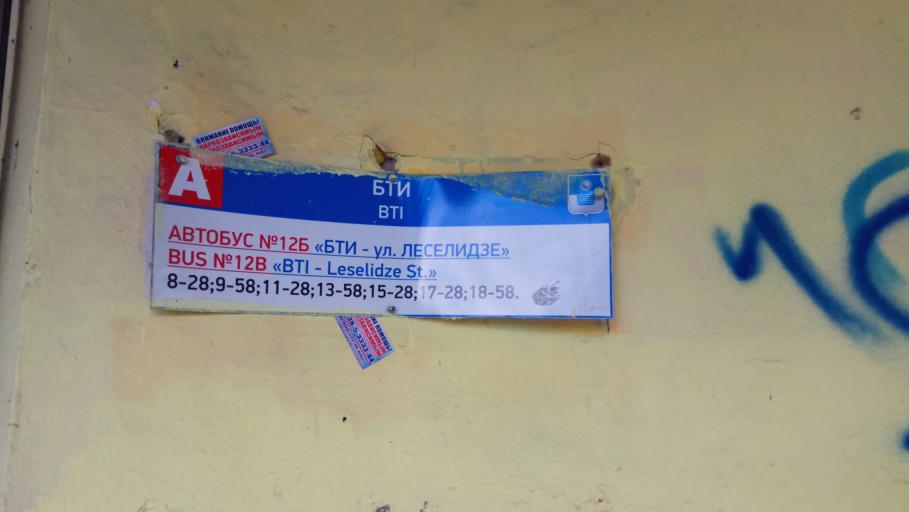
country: RU
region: Krasnodarskiy
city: Gelendzhik
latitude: 44.5531
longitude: 38.0827
